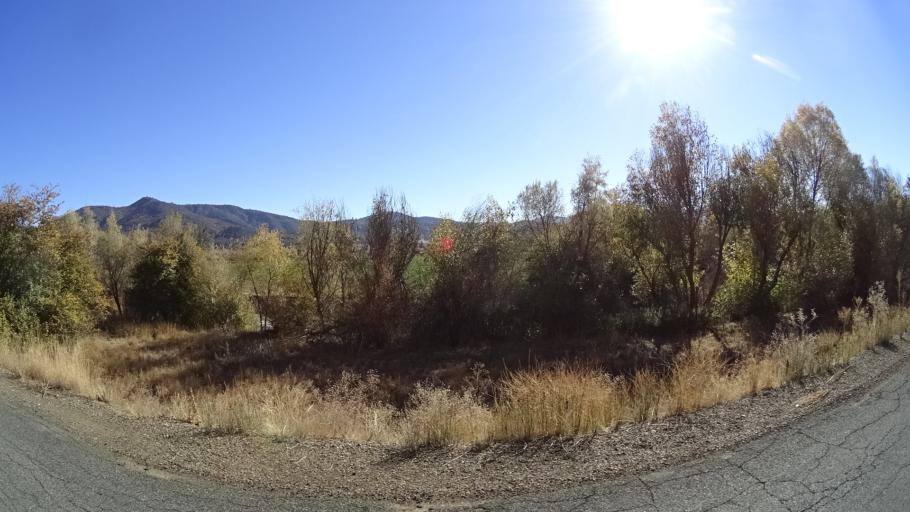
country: US
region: California
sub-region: Siskiyou County
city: Yreka
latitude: 41.5972
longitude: -122.8579
